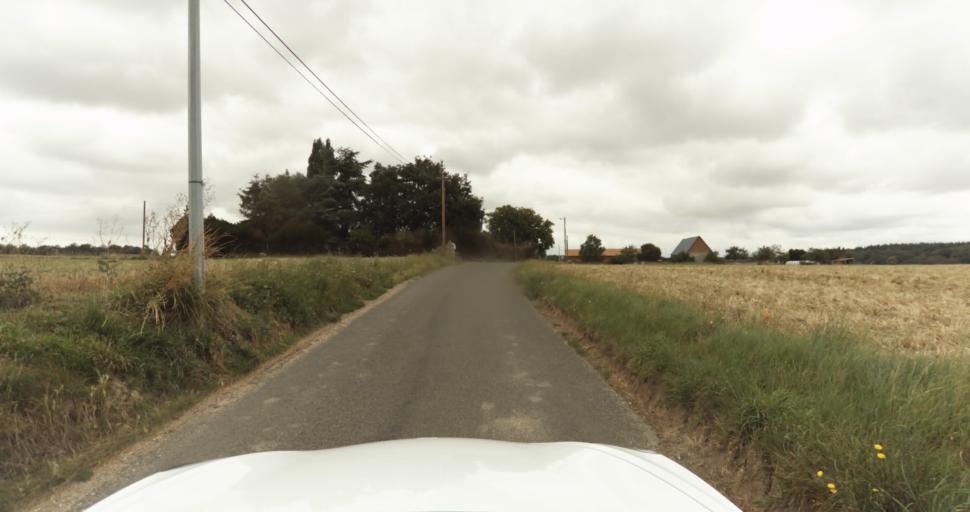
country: FR
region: Haute-Normandie
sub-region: Departement de l'Eure
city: Saint-Sebastien-de-Morsent
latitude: 49.0167
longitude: 1.0615
